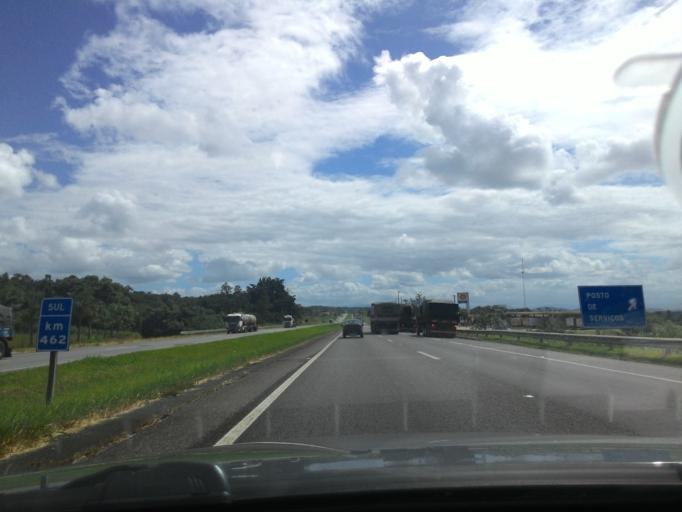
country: BR
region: Sao Paulo
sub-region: Pariquera-Acu
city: Pariquera Acu
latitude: -24.6246
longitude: -47.8979
